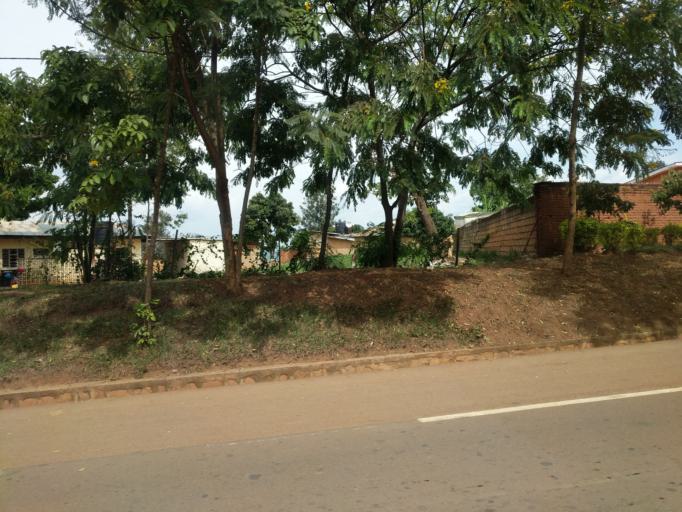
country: RW
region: Kigali
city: Kigali
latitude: -1.9719
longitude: 30.1035
